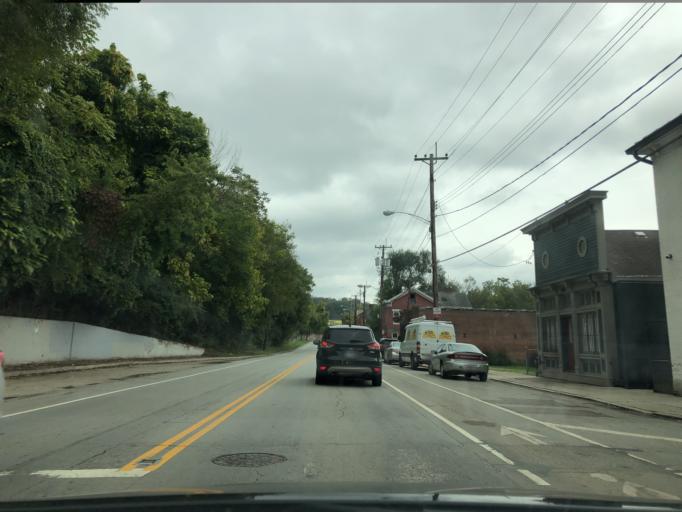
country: US
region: Kentucky
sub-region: Campbell County
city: Dayton
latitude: 39.1187
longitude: -84.4437
